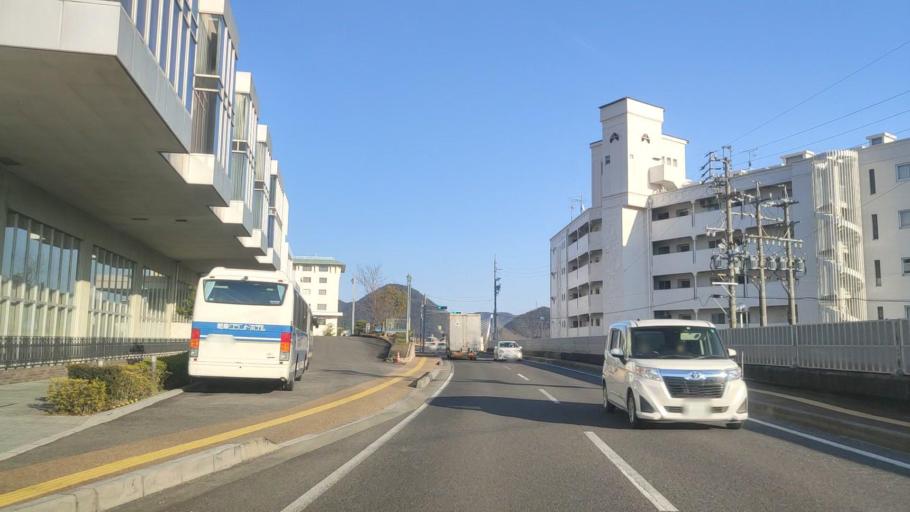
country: JP
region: Gifu
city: Gifu-shi
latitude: 35.4417
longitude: 136.7821
